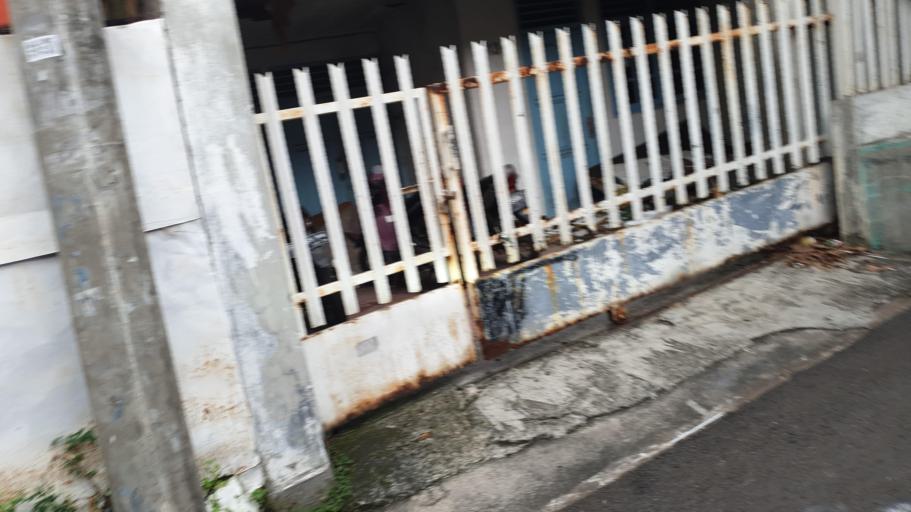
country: ID
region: Jakarta Raya
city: Jakarta
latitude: -6.2586
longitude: 106.7883
